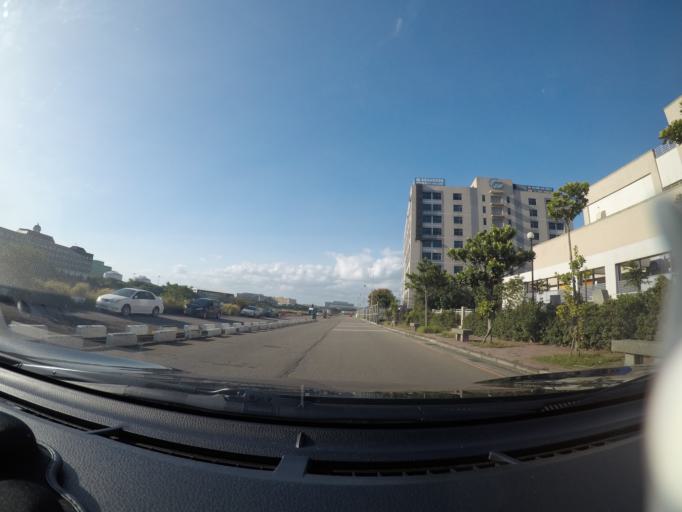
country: TW
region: Taiwan
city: Taoyuan City
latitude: 25.0922
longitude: 121.2535
